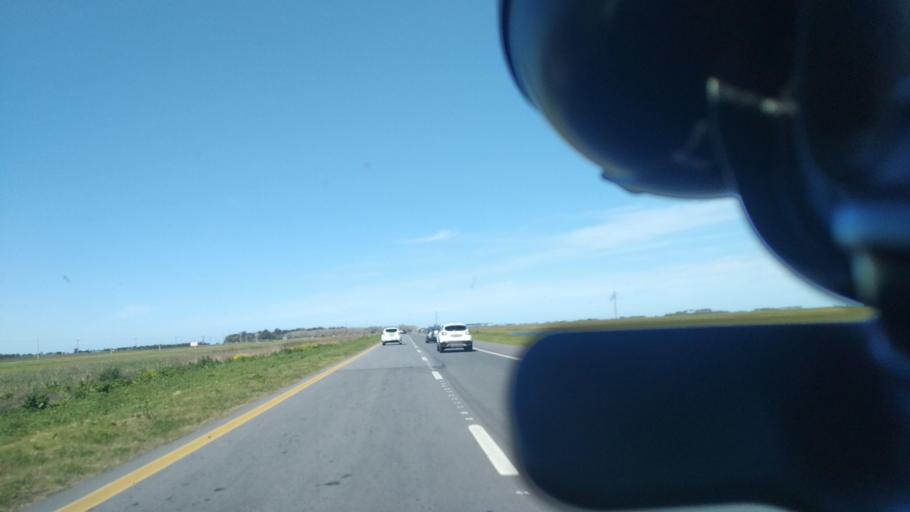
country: AR
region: Buenos Aires
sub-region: Partido de General Lavalle
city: General Lavalle
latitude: -36.4321
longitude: -56.9028
